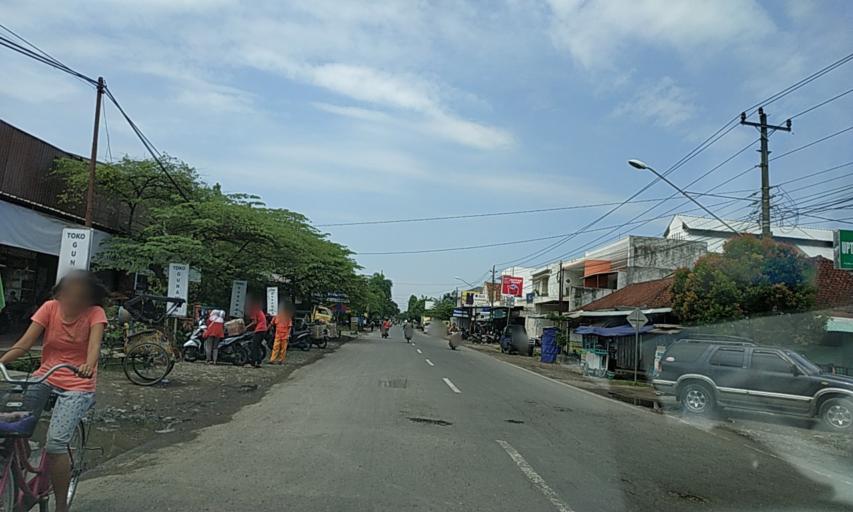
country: ID
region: Central Java
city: Sidareja
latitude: -7.4870
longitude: 108.7916
